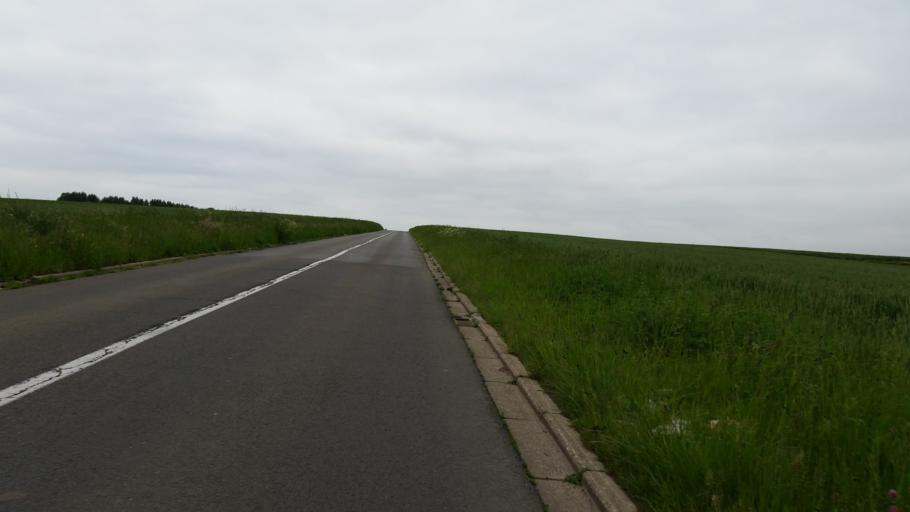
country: BE
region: Flanders
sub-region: Provincie Vlaams-Brabant
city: Grimbergen
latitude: 50.9213
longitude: 4.3811
